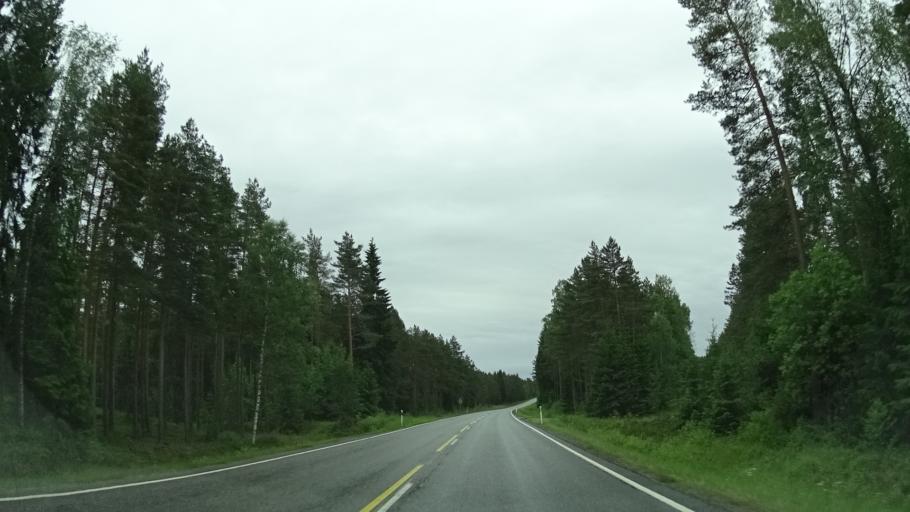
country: FI
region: Varsinais-Suomi
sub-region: Salo
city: Pernioe
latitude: 60.1153
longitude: 23.2108
